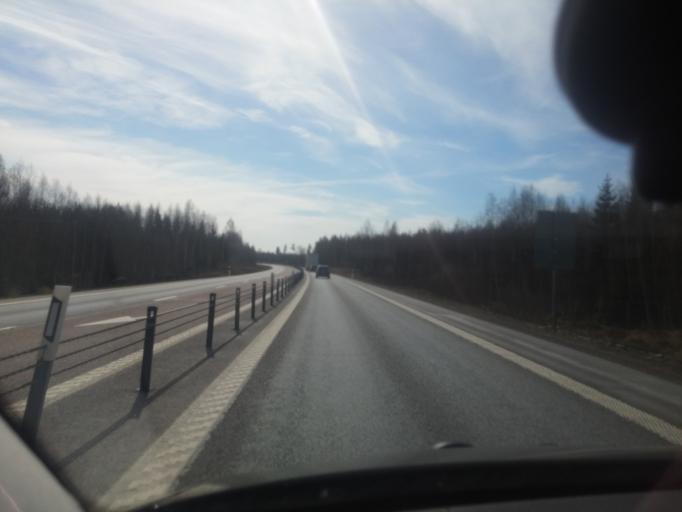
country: SE
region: Gaevleborg
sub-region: Gavle Kommun
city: Gavle
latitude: 60.7766
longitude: 17.0714
